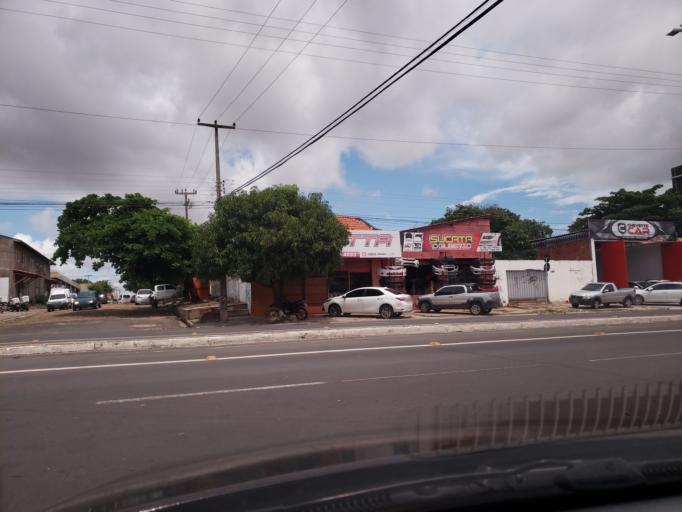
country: BR
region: Piaui
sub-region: Teresina
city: Teresina
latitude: -5.1081
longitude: -42.8083
